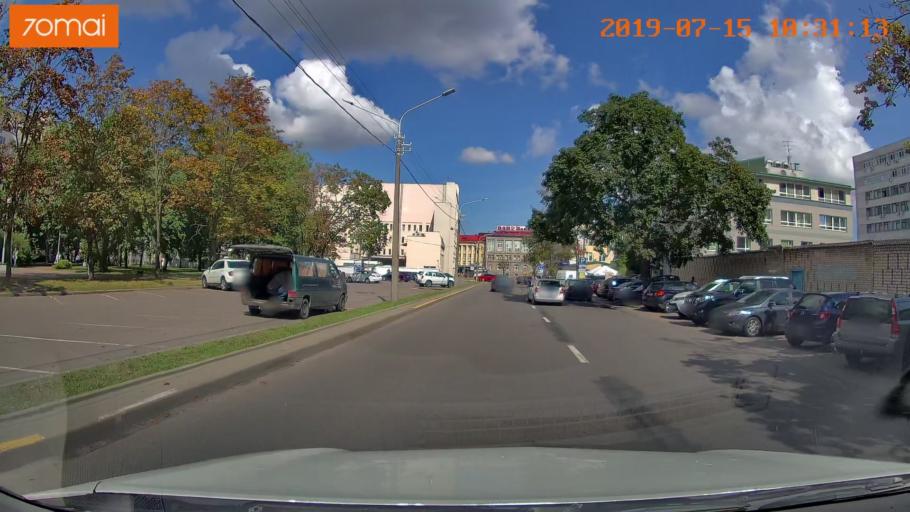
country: BY
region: Minsk
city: Minsk
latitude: 53.9155
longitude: 27.5883
